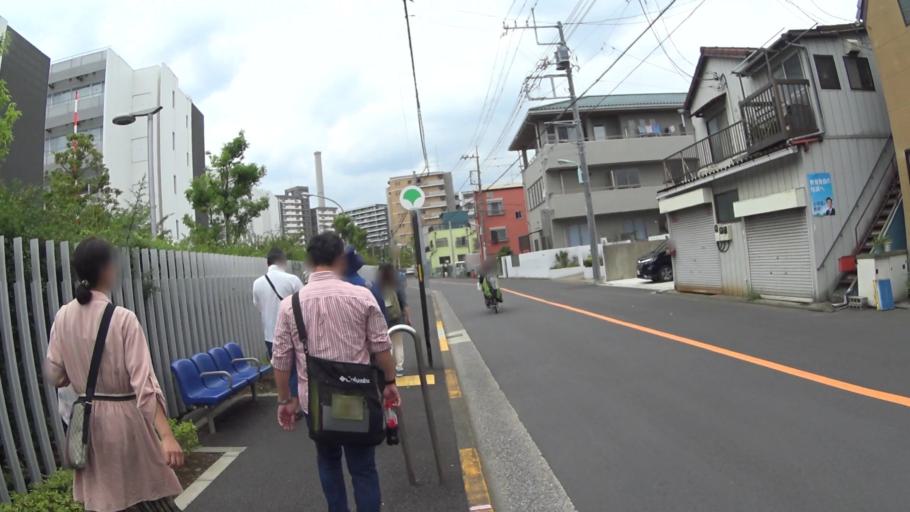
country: JP
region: Tokyo
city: Urayasu
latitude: 35.7129
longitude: 139.8379
